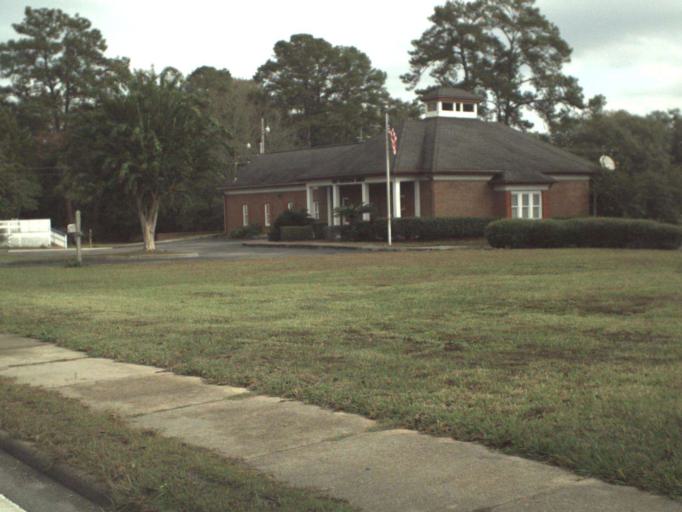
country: US
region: Florida
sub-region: Gadsden County
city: Havana
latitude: 30.6216
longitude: -84.4152
